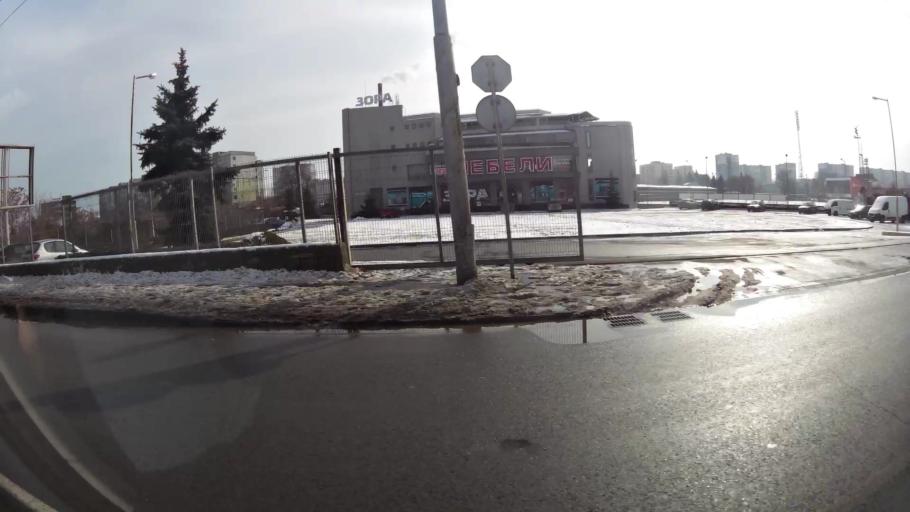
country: BG
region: Sofia-Capital
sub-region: Stolichna Obshtina
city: Sofia
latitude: 42.7082
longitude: 23.3652
